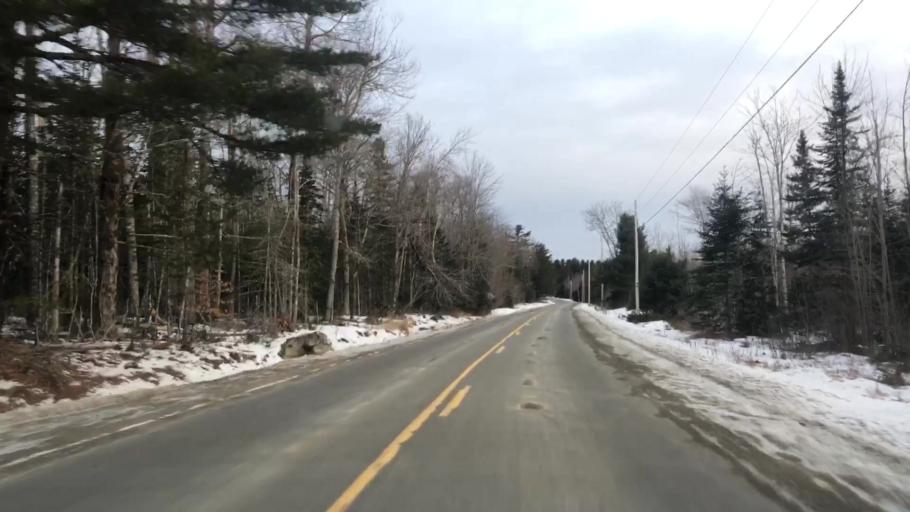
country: US
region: Maine
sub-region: Hancock County
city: Franklin
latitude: 44.7589
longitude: -68.3250
